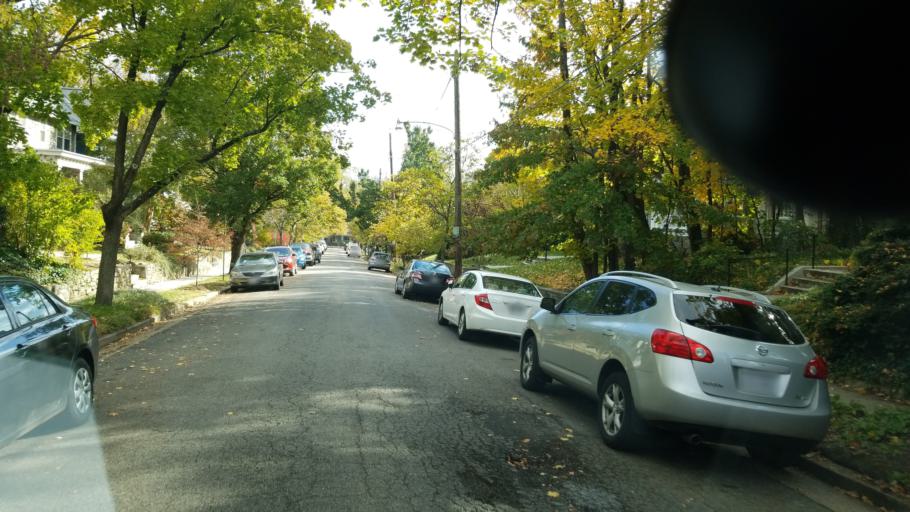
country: US
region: Maryland
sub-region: Montgomery County
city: Chevy Chase Village
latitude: 38.9658
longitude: -77.0744
